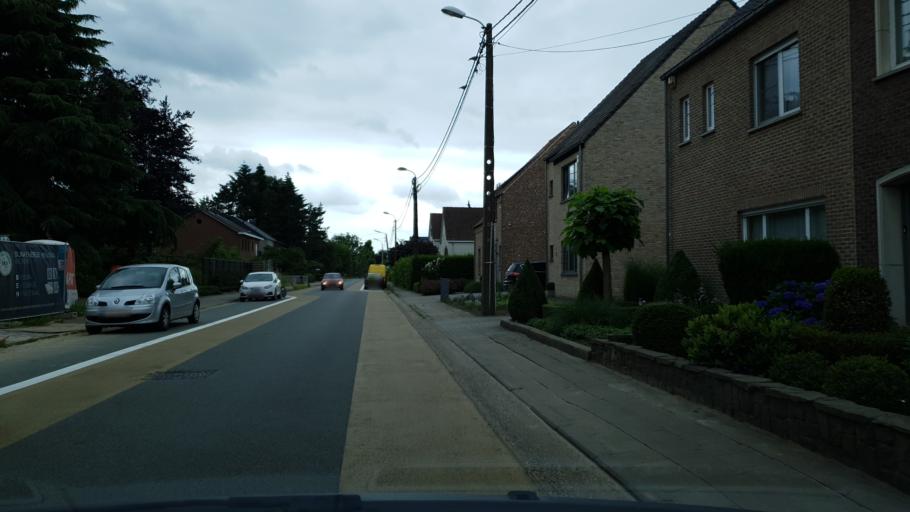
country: BE
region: Flanders
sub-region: Provincie Antwerpen
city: Geel
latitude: 51.1568
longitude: 4.9796
